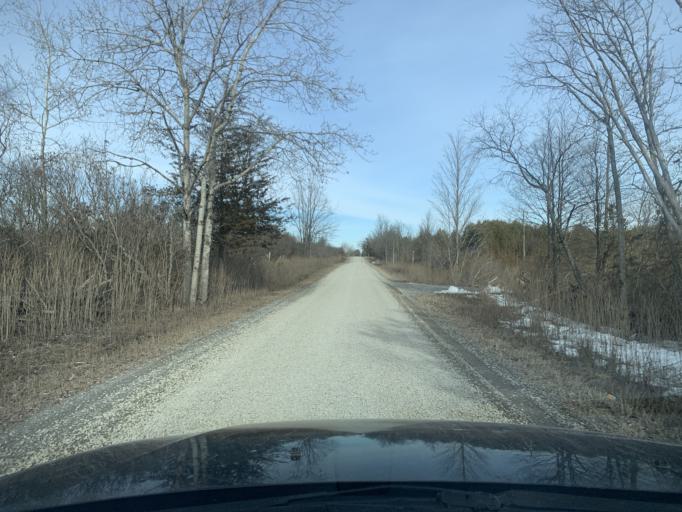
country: CA
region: Ontario
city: Deseronto
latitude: 44.3962
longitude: -77.1486
